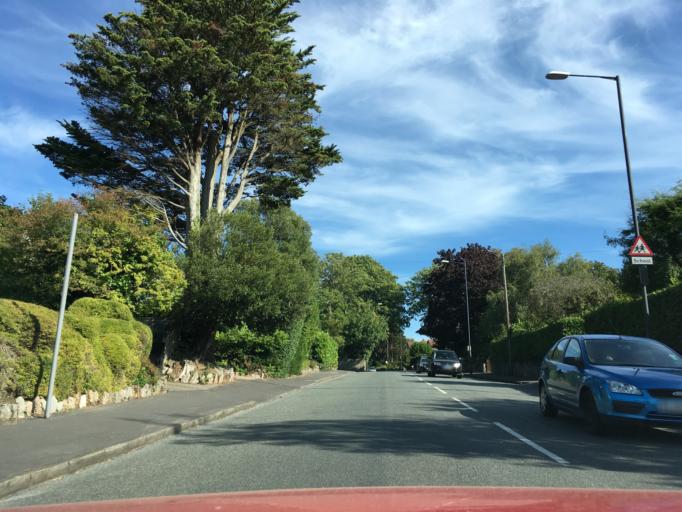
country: GB
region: England
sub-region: Bristol
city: Bristol
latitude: 51.4860
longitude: -2.6403
